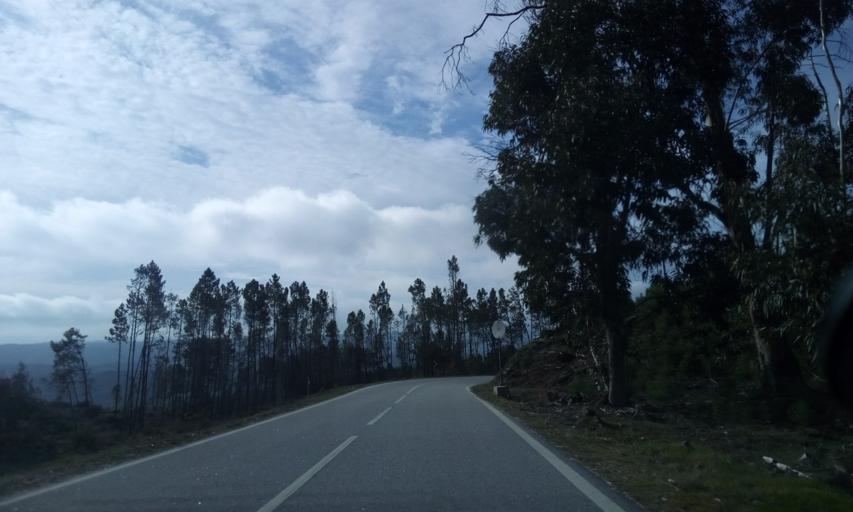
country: PT
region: Guarda
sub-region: Aguiar da Beira
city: Aguiar da Beira
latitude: 40.7479
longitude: -7.5496
